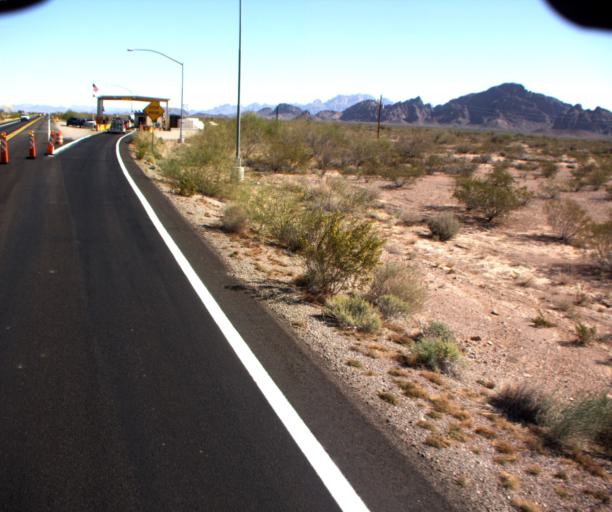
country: US
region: Arizona
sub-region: La Paz County
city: Quartzsite
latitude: 33.2584
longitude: -114.2441
